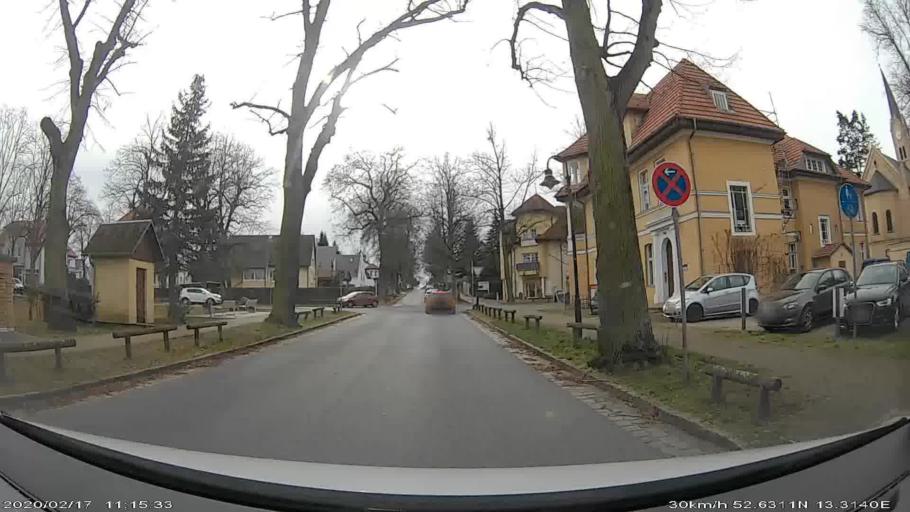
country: DE
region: Brandenburg
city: Glienicke
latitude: 52.6311
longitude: 13.3141
